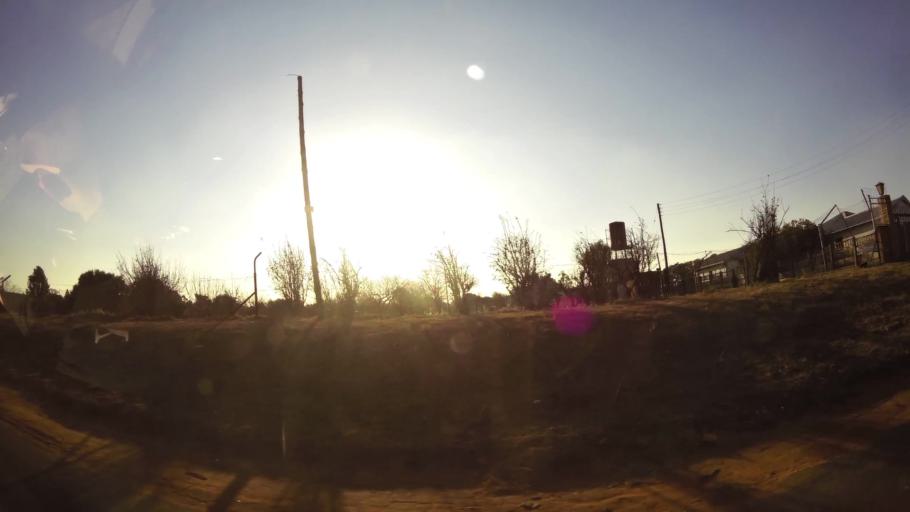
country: ZA
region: Gauteng
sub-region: West Rand District Municipality
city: Randfontein
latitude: -26.2177
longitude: 27.6516
